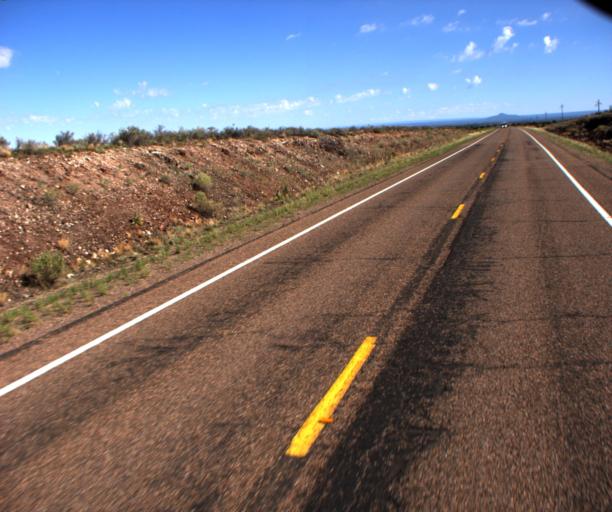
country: US
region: Arizona
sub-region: Coconino County
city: Williams
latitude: 35.5392
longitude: -112.1634
